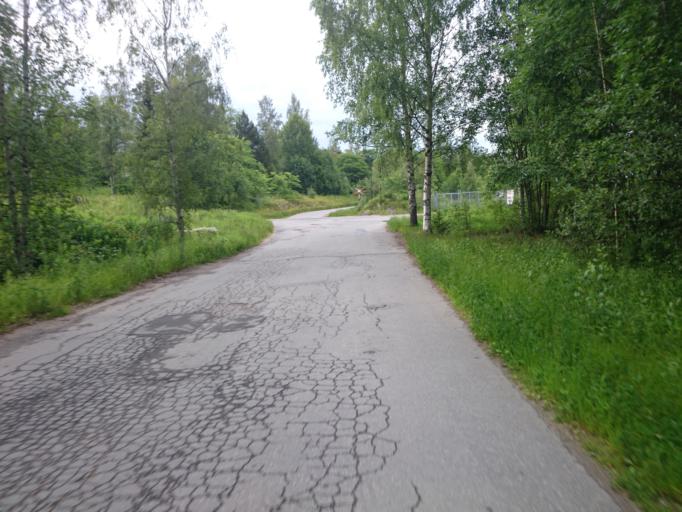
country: SE
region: Vaesternorrland
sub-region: Sundsvalls Kommun
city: Kvissleby
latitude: 62.3141
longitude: 17.3712
